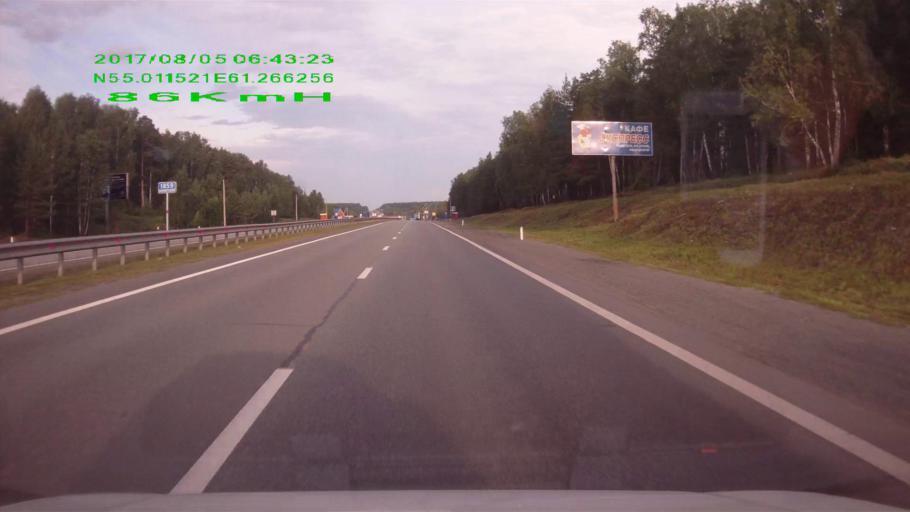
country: RU
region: Chelyabinsk
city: Sargazy
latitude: 55.0115
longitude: 61.2659
